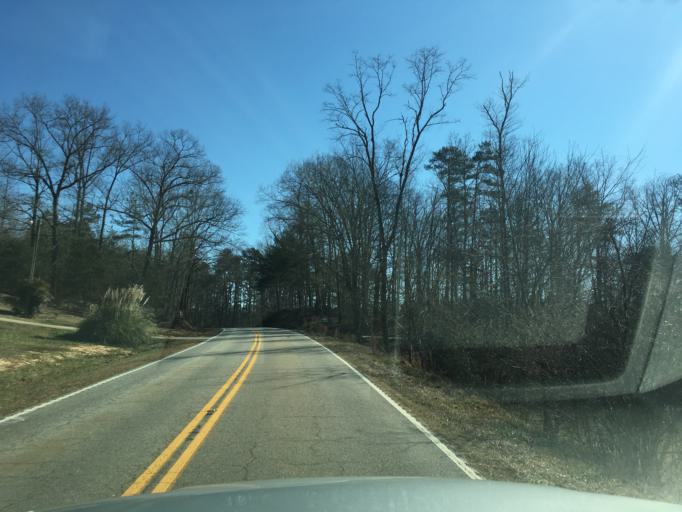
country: US
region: South Carolina
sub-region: Pickens County
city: Liberty
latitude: 34.7934
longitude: -82.7288
